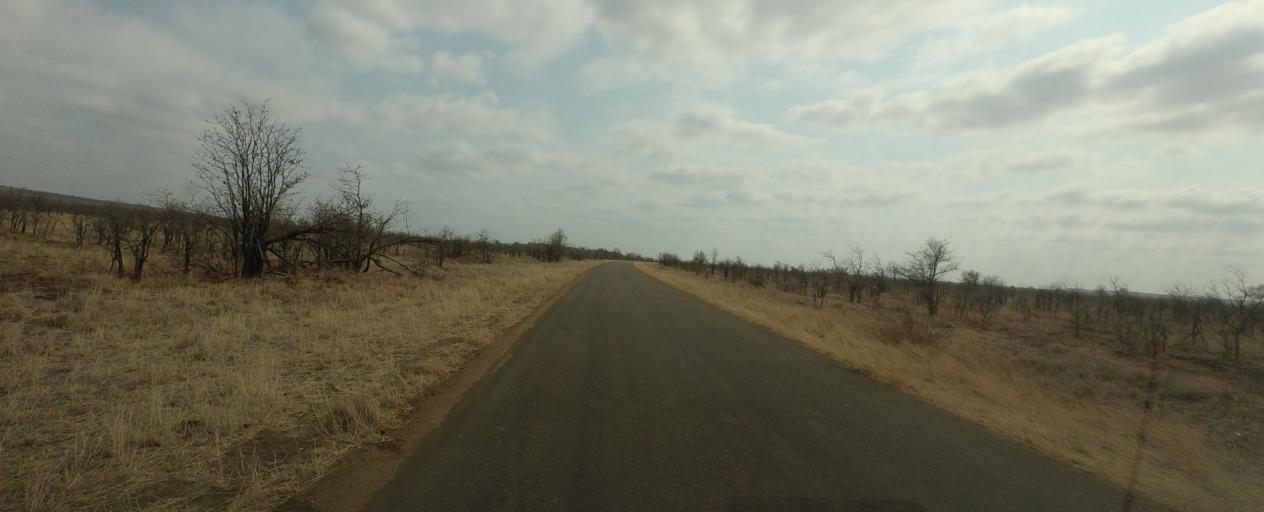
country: ZA
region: Limpopo
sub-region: Vhembe District Municipality
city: Mutale
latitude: -22.6088
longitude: 31.1740
